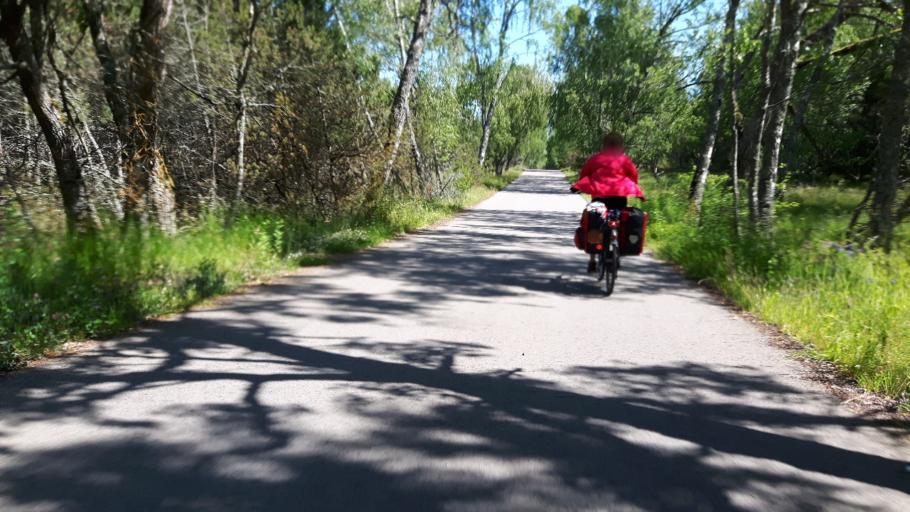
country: LT
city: Neringa
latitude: 55.4110
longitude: 21.0877
